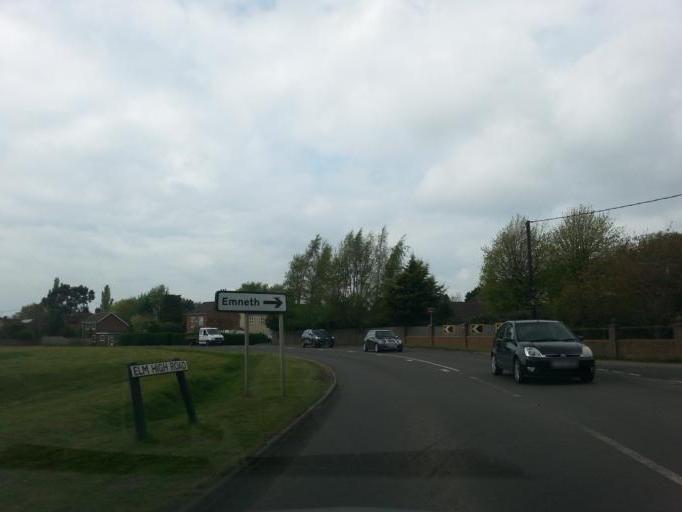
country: GB
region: England
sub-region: Norfolk
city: Emneth
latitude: 52.6449
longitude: 0.1841
